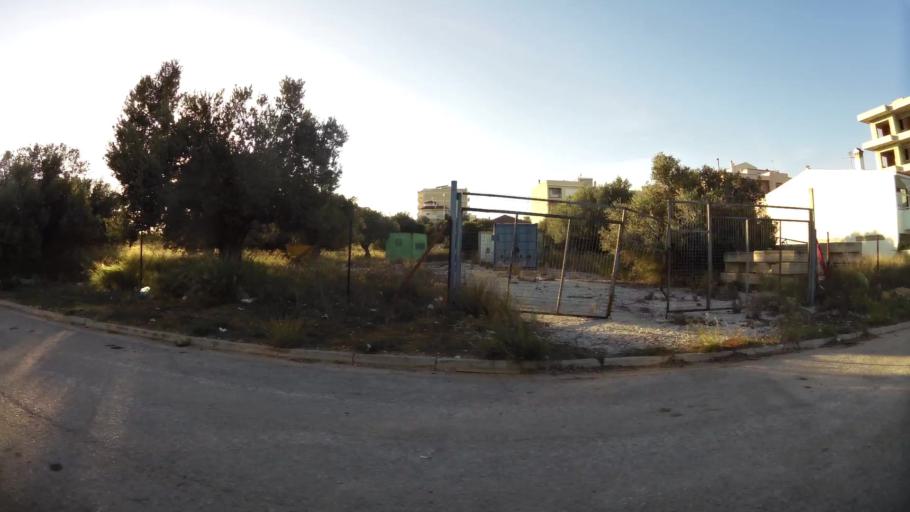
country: GR
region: Attica
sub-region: Nomarchia Anatolikis Attikis
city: Spata
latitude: 37.9585
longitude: 23.9264
